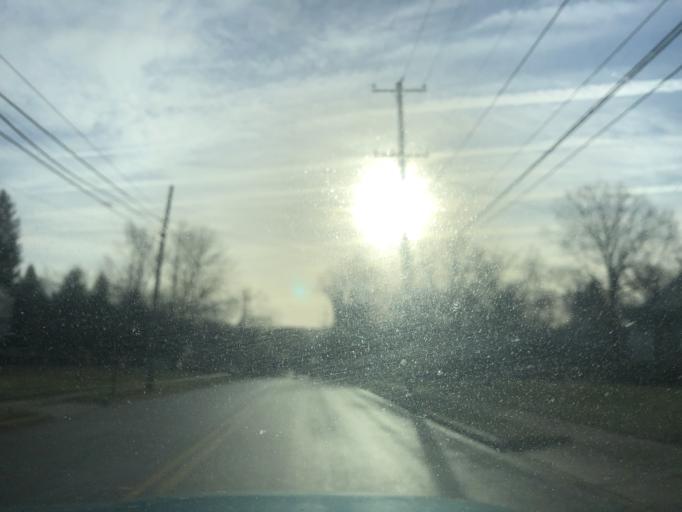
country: US
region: Pennsylvania
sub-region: Montgomery County
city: Fort Washington
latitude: 40.1431
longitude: -75.1952
